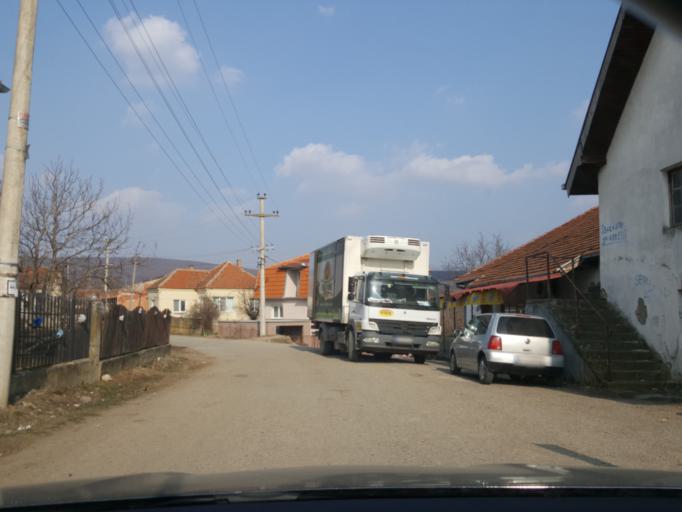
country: RS
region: Central Serbia
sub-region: Nisavski Okrug
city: Aleksinac
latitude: 43.5290
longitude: 21.7377
